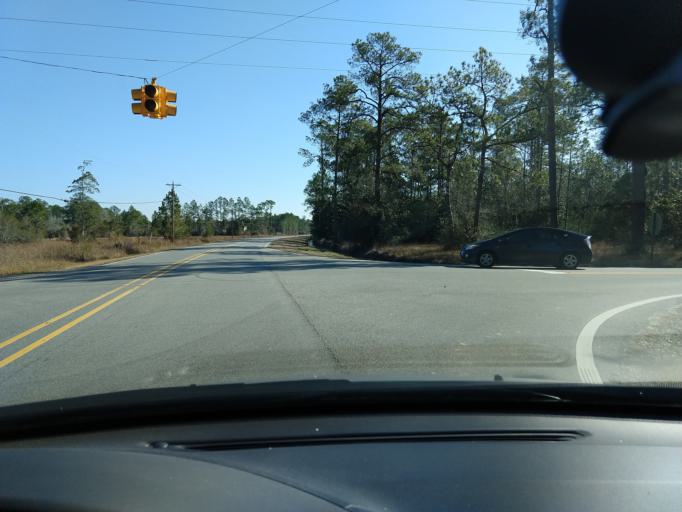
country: US
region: Alabama
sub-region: Mobile County
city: Grand Bay
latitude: 30.4725
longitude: -88.4204
